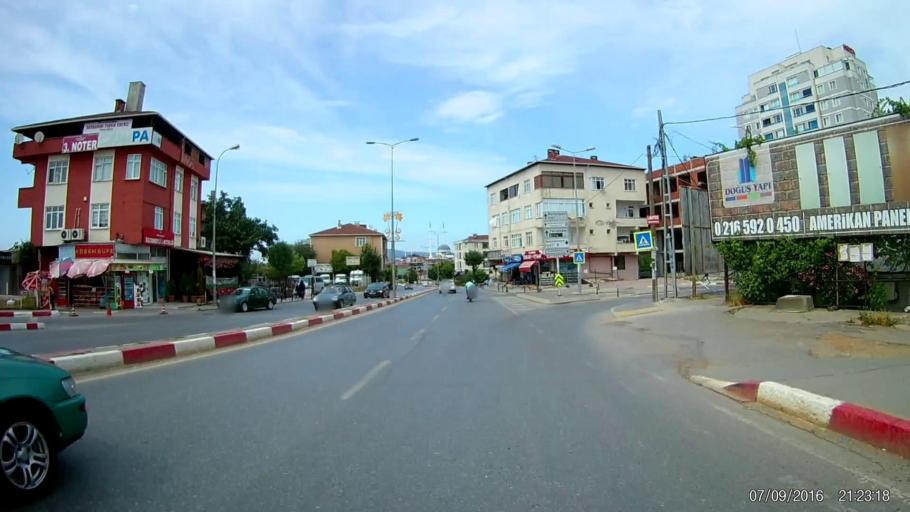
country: TR
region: Istanbul
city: Sultanbeyli
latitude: 40.9725
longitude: 29.2630
